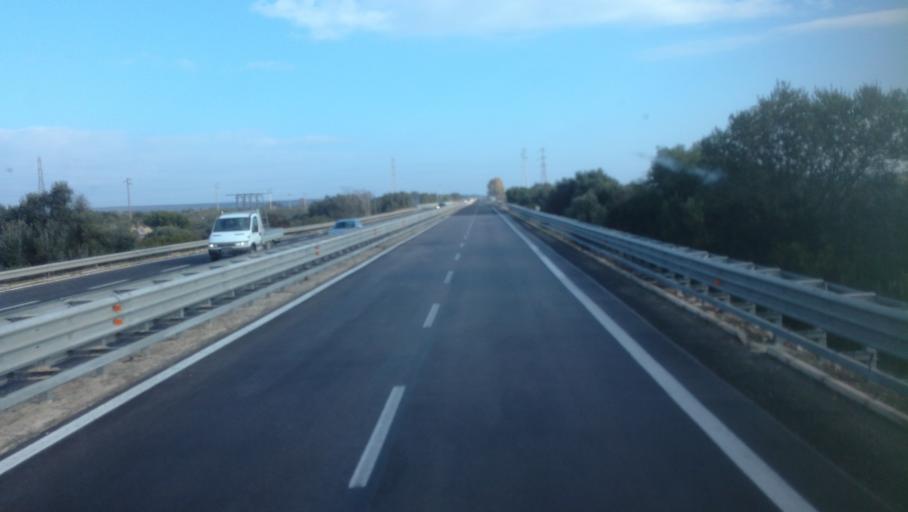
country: IT
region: Apulia
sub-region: Provincia di Taranto
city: Paolo VI
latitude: 40.5370
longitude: 17.2705
